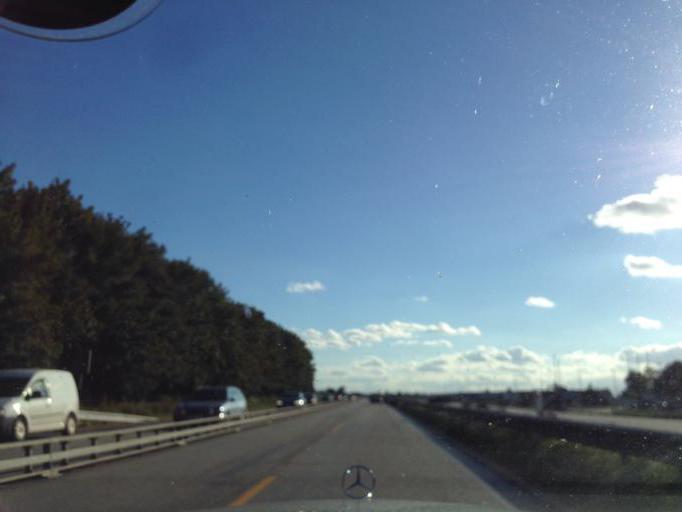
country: DE
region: Schleswig-Holstein
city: Krogaspe
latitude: 54.0938
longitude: 9.9321
